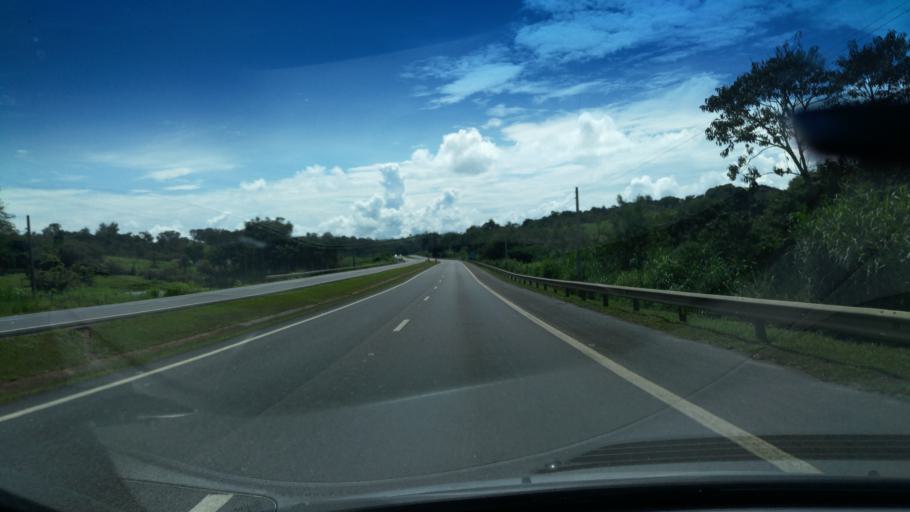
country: BR
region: Sao Paulo
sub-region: Santo Antonio Do Jardim
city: Espirito Santo do Pinhal
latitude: -22.2329
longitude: -46.7969
